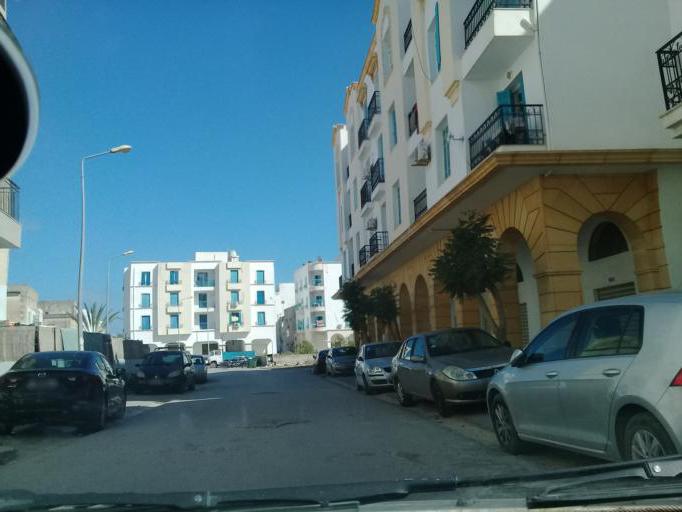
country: TN
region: Tunis
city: La Goulette
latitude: 36.8162
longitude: 10.3007
